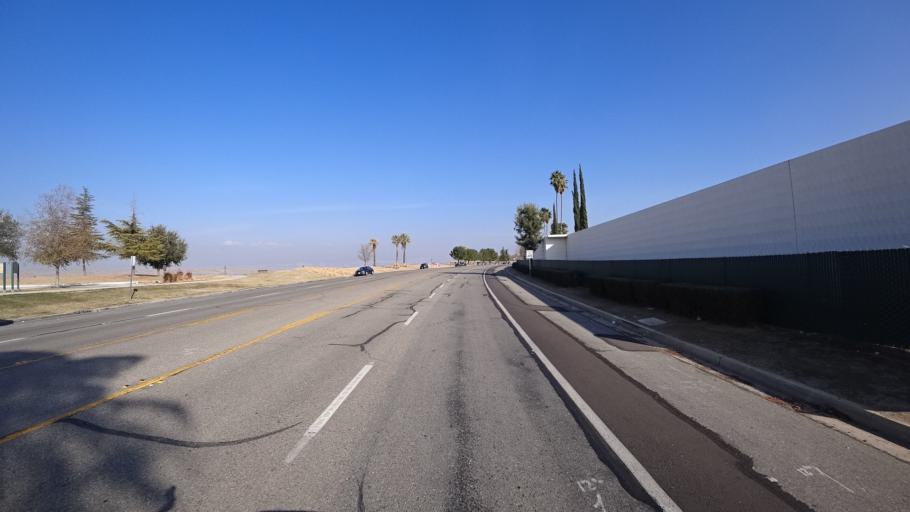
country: US
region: California
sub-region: Kern County
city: Oildale
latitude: 35.4087
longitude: -118.9899
